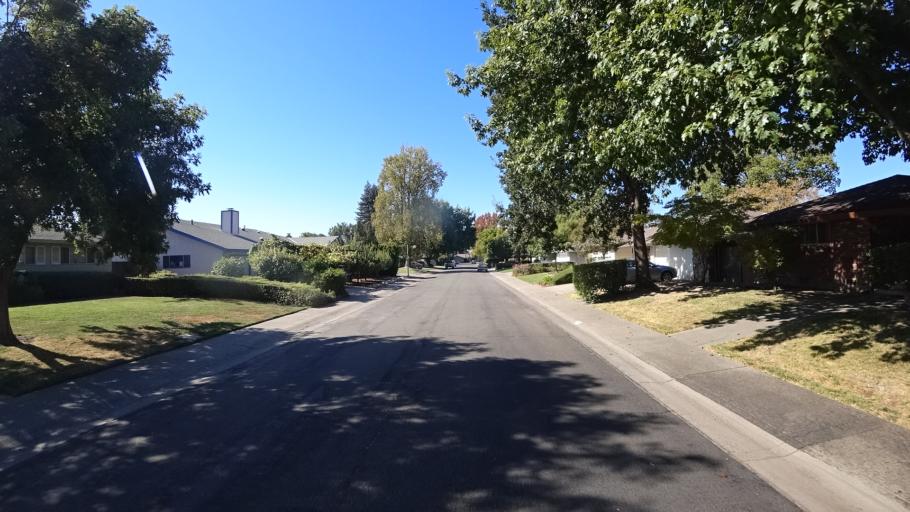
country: US
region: California
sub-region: Sacramento County
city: Parkway
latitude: 38.5079
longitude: -121.5289
